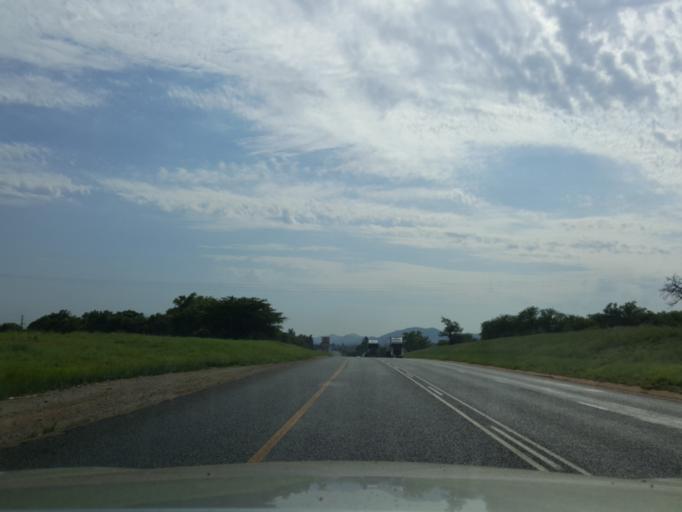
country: SZ
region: Hhohho
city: Ntfonjeni
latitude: -25.5155
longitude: 31.4499
